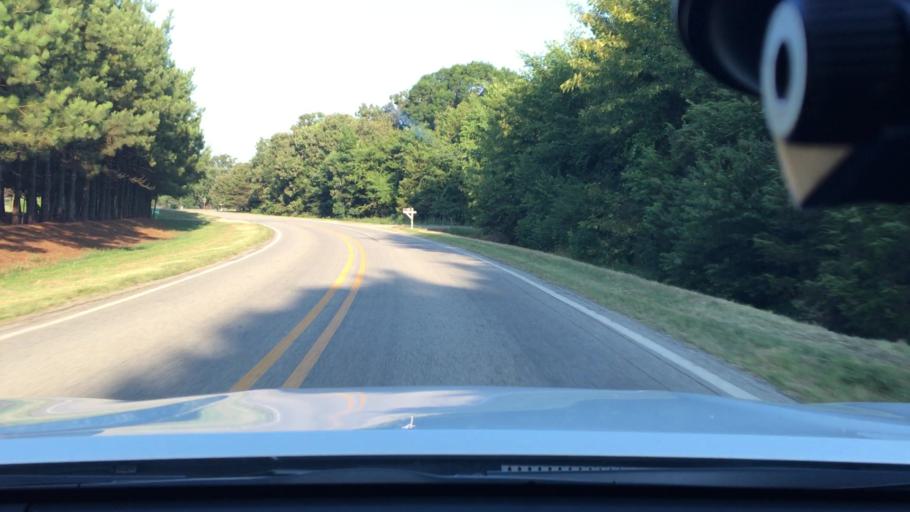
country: US
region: Arkansas
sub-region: Johnson County
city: Coal Hill
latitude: 35.3576
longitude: -93.5597
